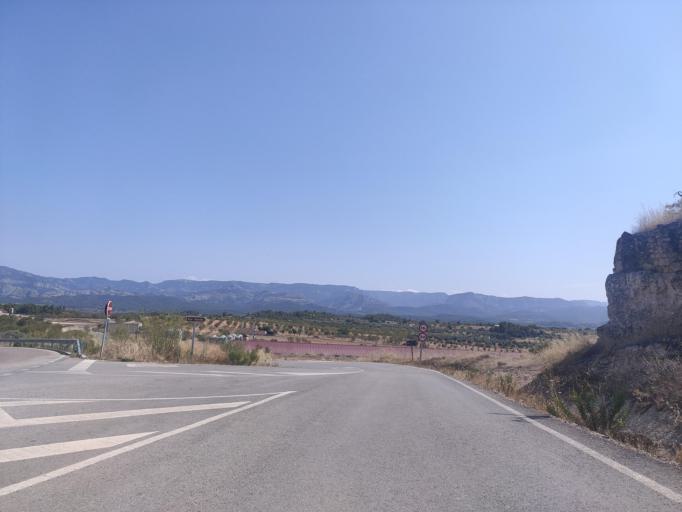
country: ES
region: Aragon
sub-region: Provincia de Teruel
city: Lledo
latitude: 40.9277
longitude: 0.2168
